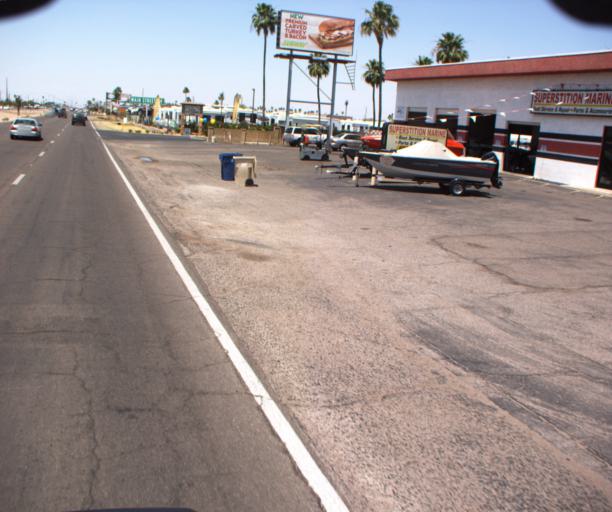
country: US
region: Arizona
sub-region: Pinal County
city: Apache Junction
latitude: 33.4154
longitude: -111.5926
